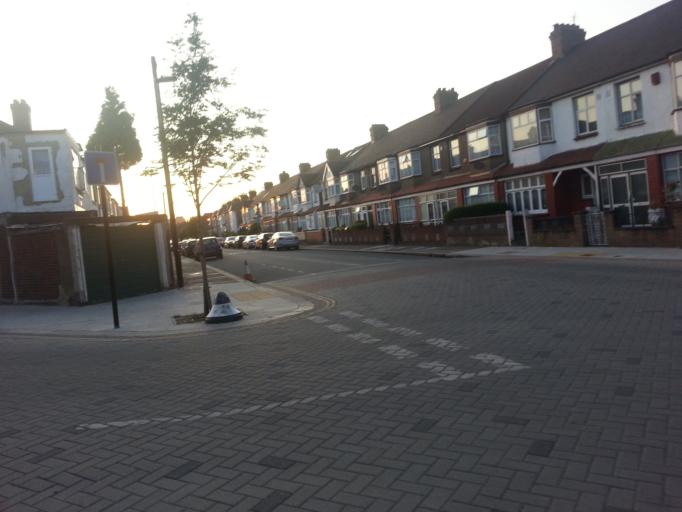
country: GB
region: England
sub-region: Greater London
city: Harringay
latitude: 51.5906
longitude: -0.0960
